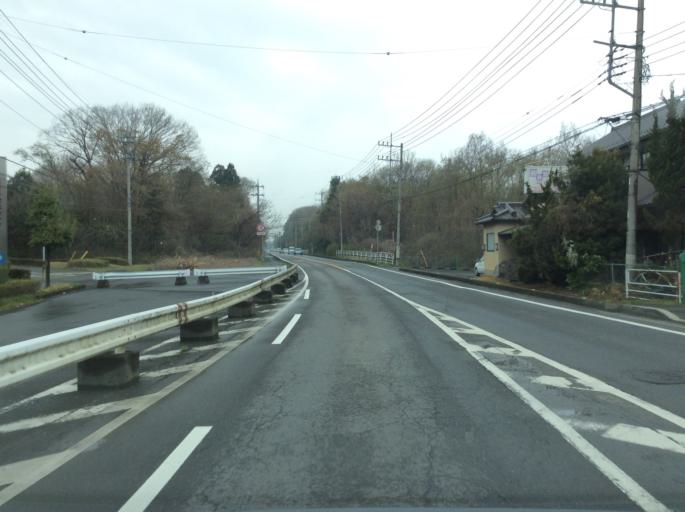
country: JP
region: Ibaraki
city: Mitsukaido
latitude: 35.9848
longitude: 139.9588
